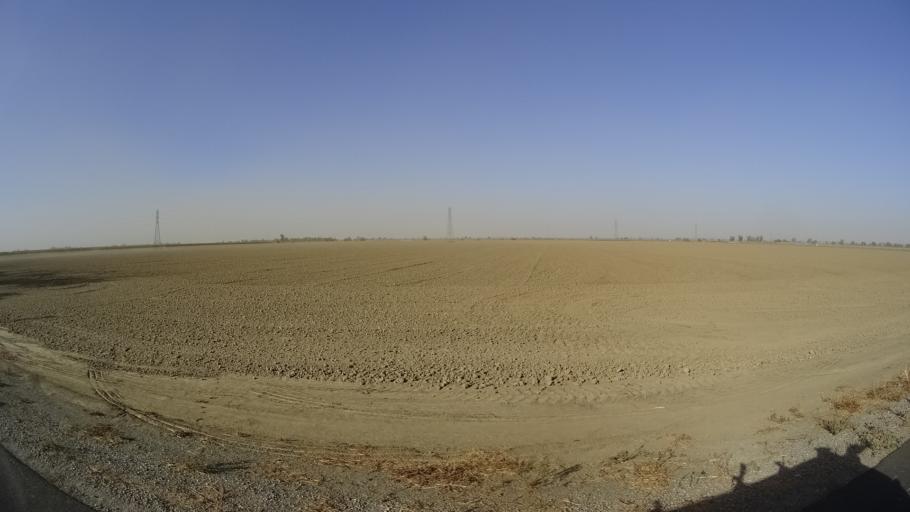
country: US
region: California
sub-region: Yolo County
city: Woodland
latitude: 38.7931
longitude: -121.7705
